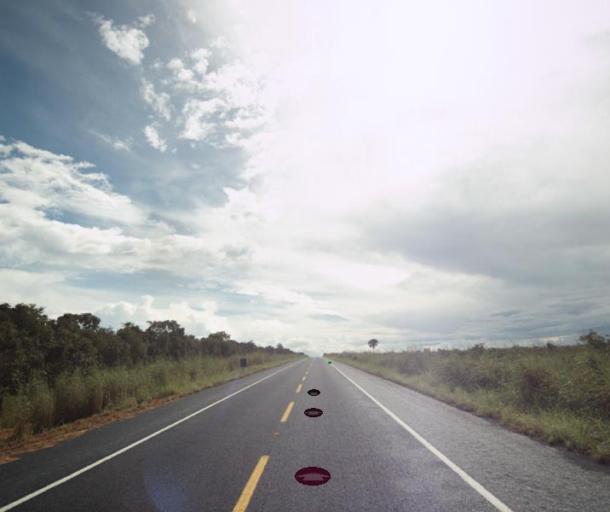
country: BR
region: Goias
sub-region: Sao Miguel Do Araguaia
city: Sao Miguel do Araguaia
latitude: -13.2930
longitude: -50.3930
